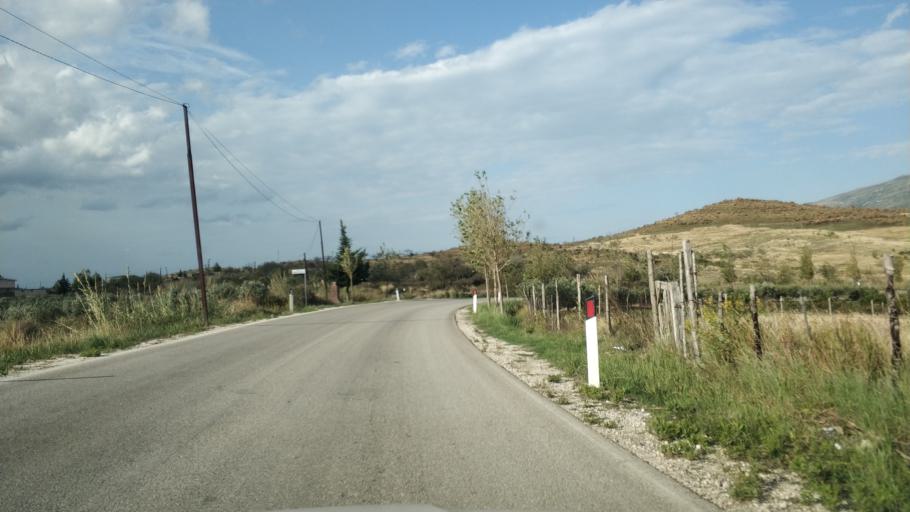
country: AL
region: Vlore
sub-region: Rrethi i Vlores
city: Orikum
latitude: 40.3103
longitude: 19.4801
